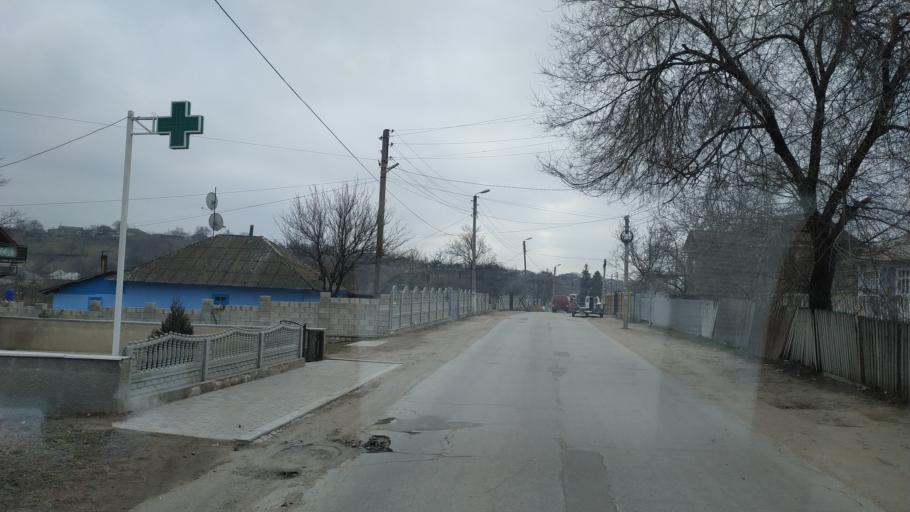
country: MD
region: Hincesti
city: Hincesti
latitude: 46.8806
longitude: 28.4109
